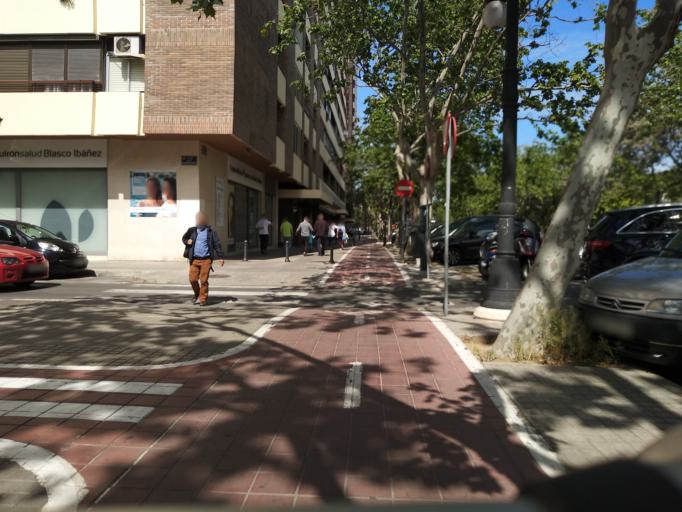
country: ES
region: Valencia
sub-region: Provincia de Valencia
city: Valencia
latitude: 39.4785
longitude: -0.3646
